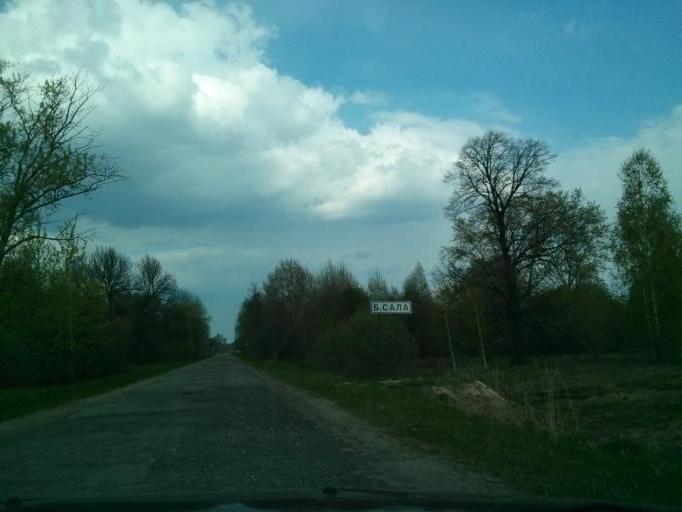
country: RU
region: Nizjnij Novgorod
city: Shimorskoye
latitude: 55.3023
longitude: 41.8358
